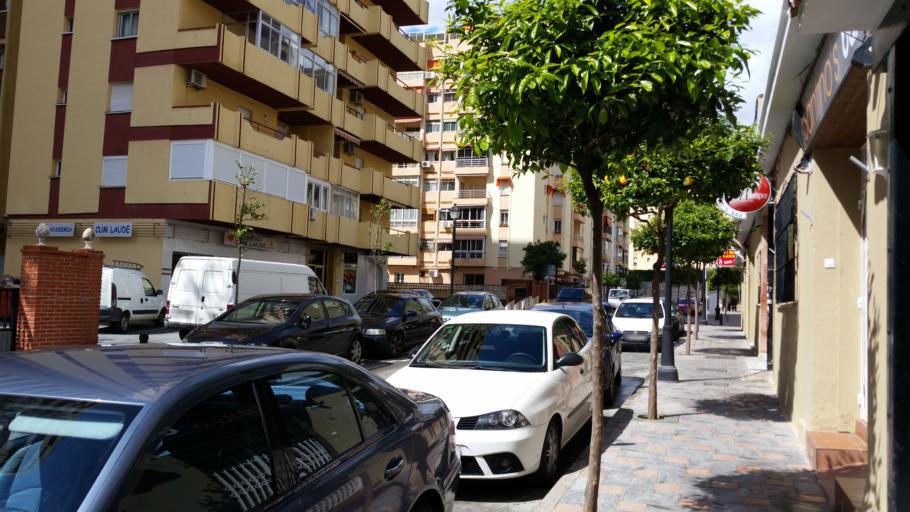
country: ES
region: Andalusia
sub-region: Provincia de Malaga
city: Fuengirola
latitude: 36.5530
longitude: -4.6174
